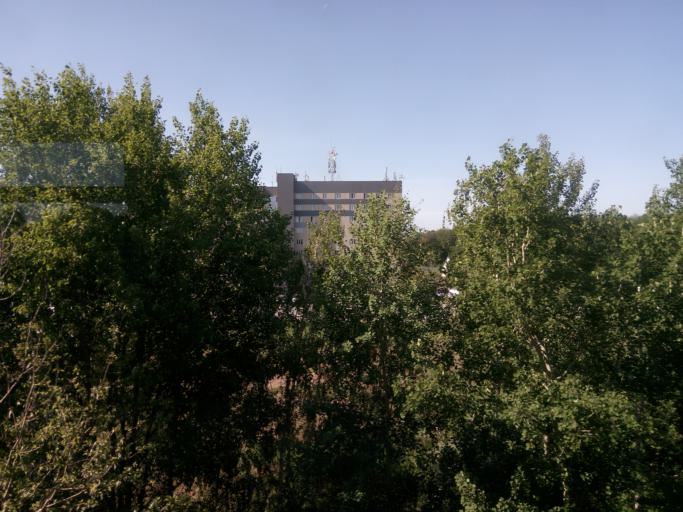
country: RU
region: Tatarstan
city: Stolbishchi
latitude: 55.6117
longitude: 49.2931
